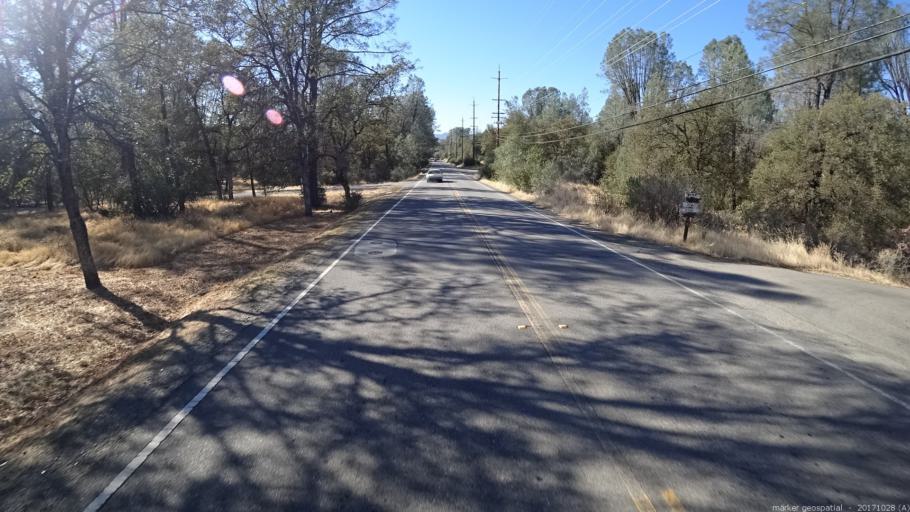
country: US
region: California
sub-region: Shasta County
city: Redding
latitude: 40.6258
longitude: -122.4091
